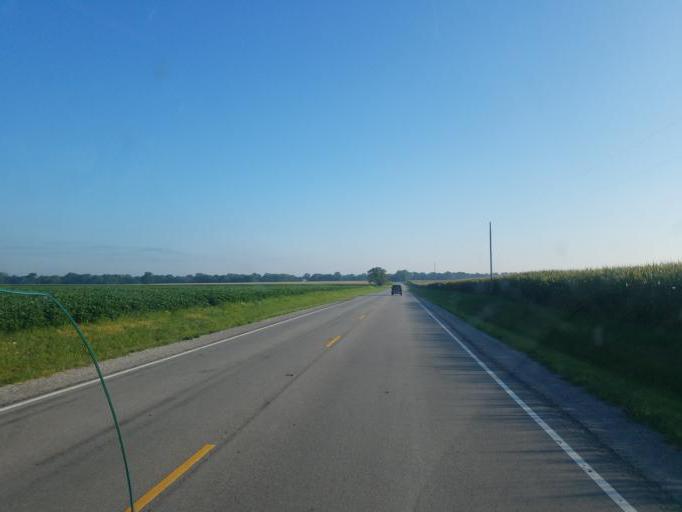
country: US
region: Illinois
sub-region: Bond County
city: Greenville
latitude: 38.8510
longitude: -89.3713
